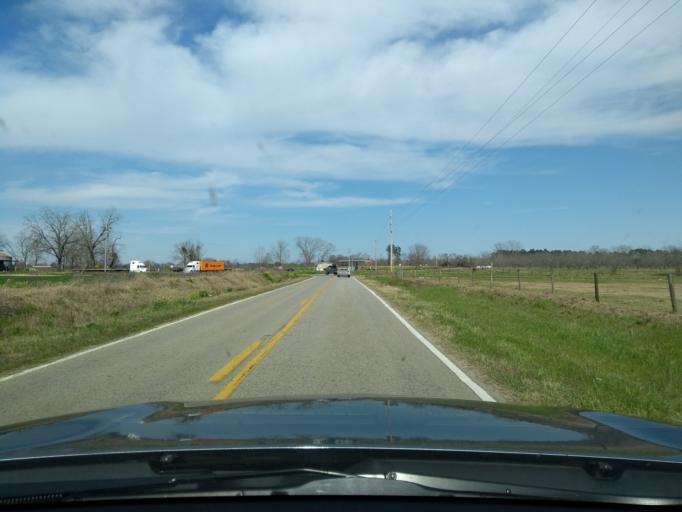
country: US
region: Georgia
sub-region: Bulloch County
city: Brooklet
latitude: 32.4576
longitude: -81.6594
